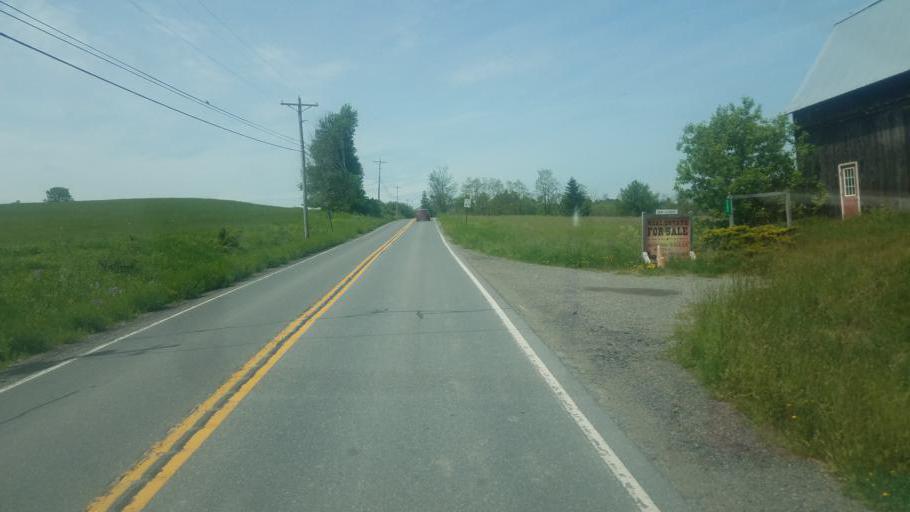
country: US
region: Pennsylvania
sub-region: Tioga County
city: Wellsboro
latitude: 41.7702
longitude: -77.1929
